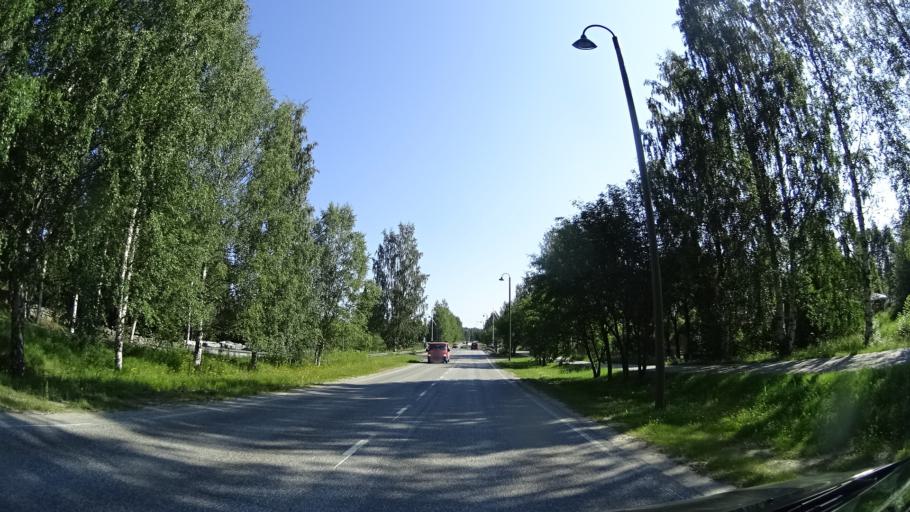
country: FI
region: North Karelia
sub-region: Joensuu
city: Juuka
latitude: 63.2447
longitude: 29.2589
